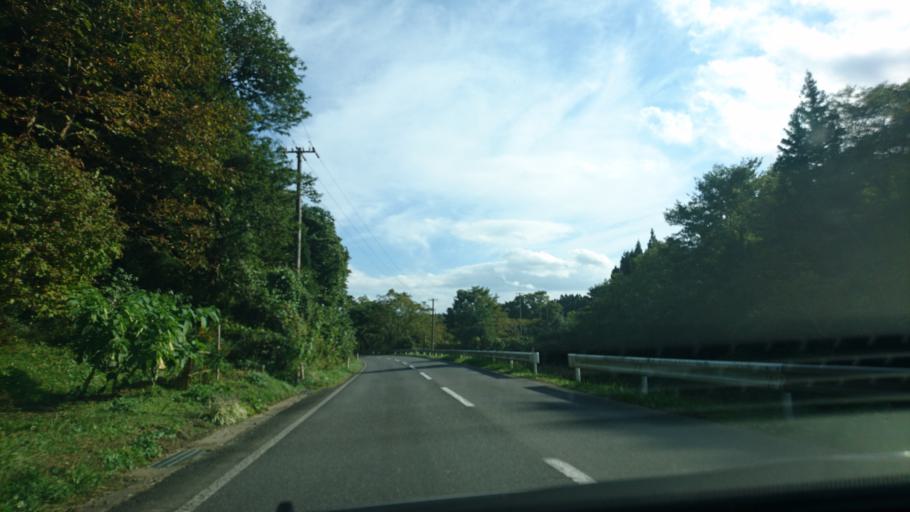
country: JP
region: Iwate
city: Ichinoseki
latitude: 38.8592
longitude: 141.3315
